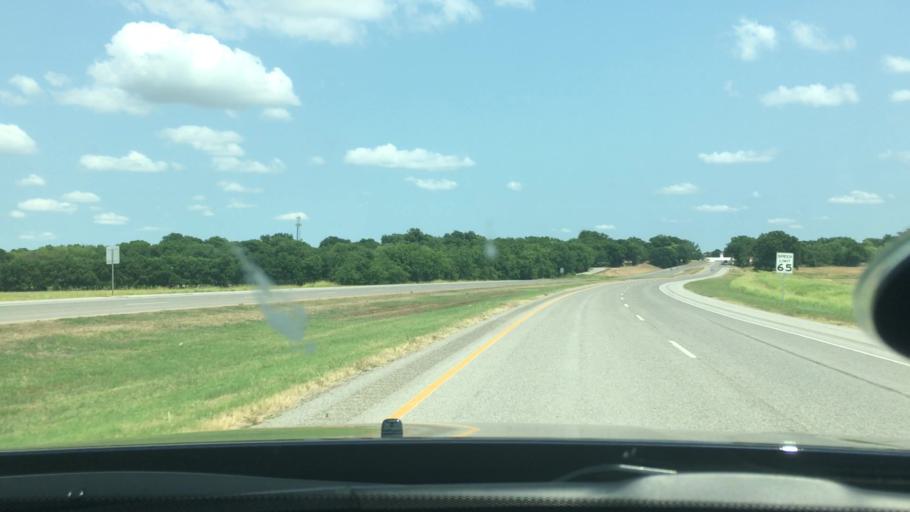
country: US
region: Oklahoma
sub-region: Murray County
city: Davis
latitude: 34.5045
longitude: -97.1351
